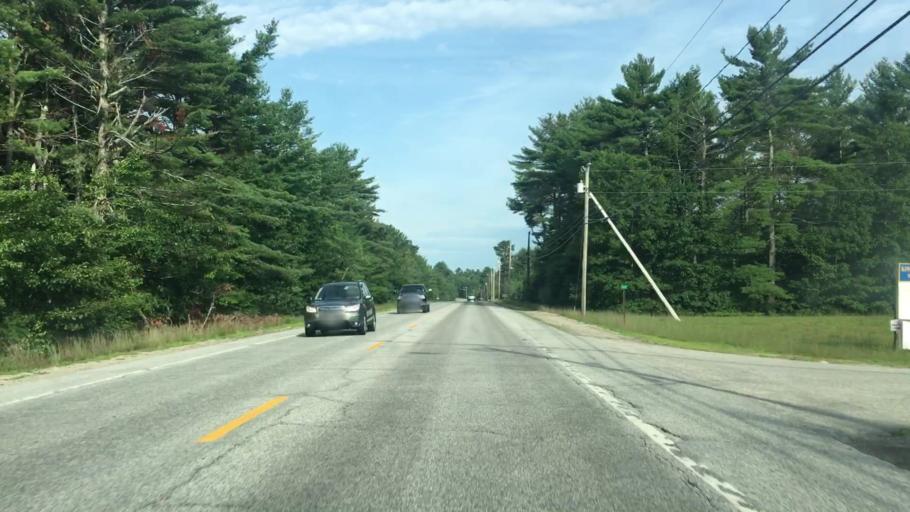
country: US
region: Maine
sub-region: Cumberland County
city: Steep Falls
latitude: 43.7348
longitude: -70.6210
